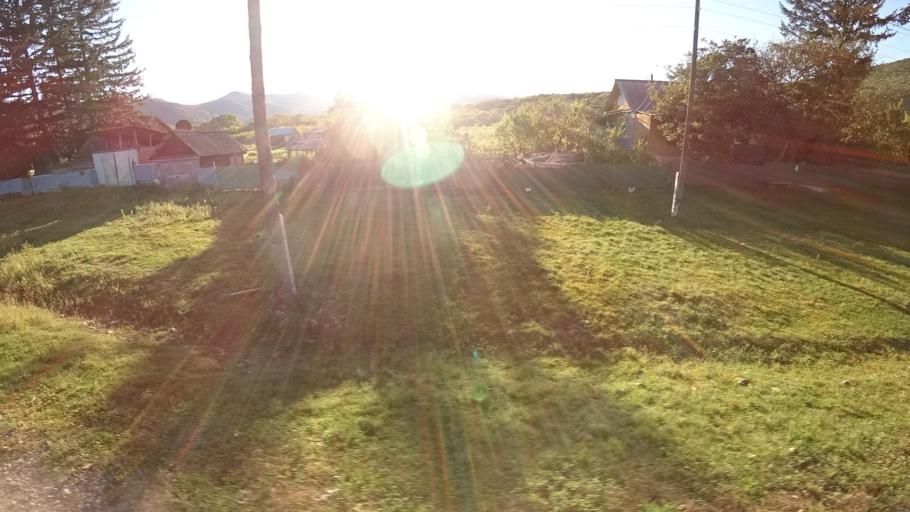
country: RU
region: Primorskiy
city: Kirovskiy
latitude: 44.8310
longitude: 133.5727
